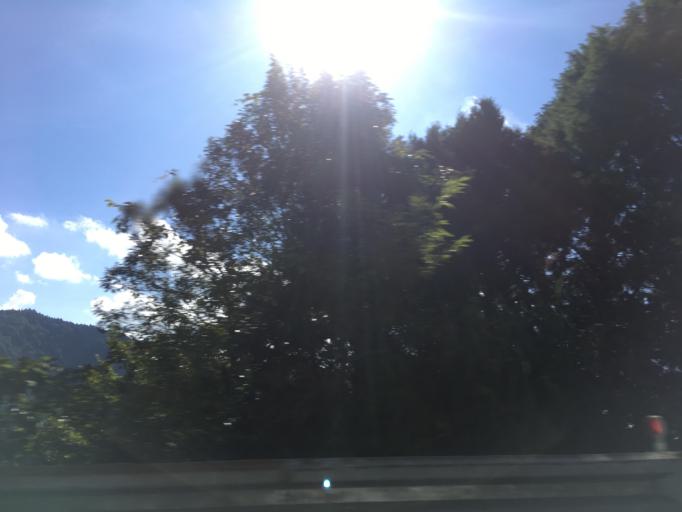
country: TW
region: Taiwan
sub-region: Yilan
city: Yilan
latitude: 24.5054
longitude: 121.5694
